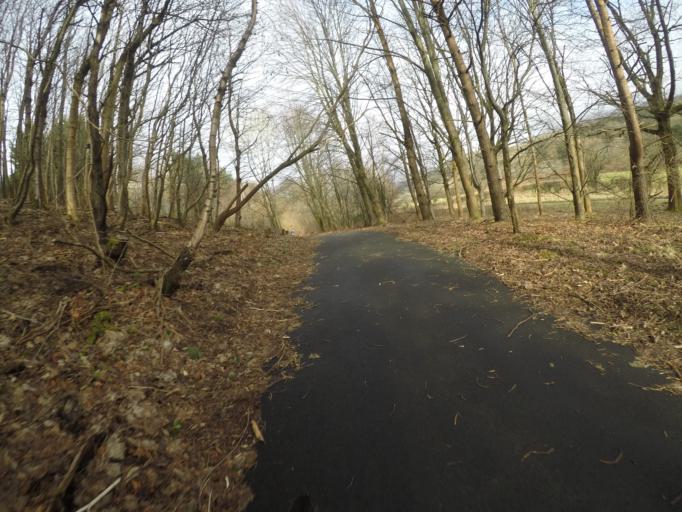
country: GB
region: Scotland
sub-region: North Ayrshire
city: Fairlie
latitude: 55.7387
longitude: -4.8616
